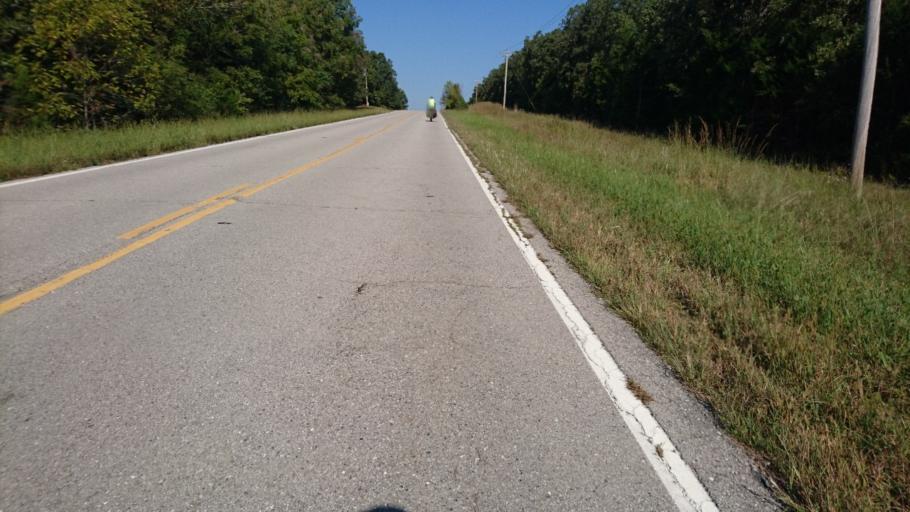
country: US
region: Missouri
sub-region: Pulaski County
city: Richland
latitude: 37.7615
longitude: -92.3781
